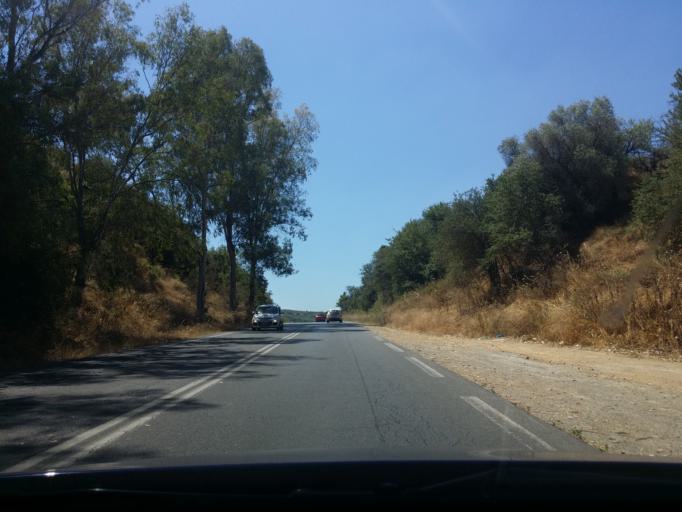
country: GR
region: Peloponnese
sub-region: Nomos Lakonias
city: Krokeai
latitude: 36.9523
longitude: 22.5102
